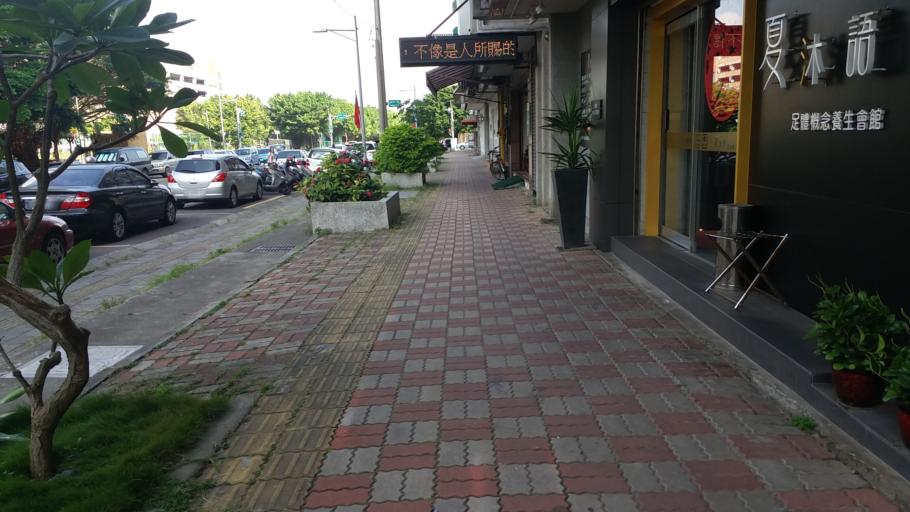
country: TW
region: Taiwan
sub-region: Hsinchu
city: Hsinchu
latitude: 24.8021
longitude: 120.9931
